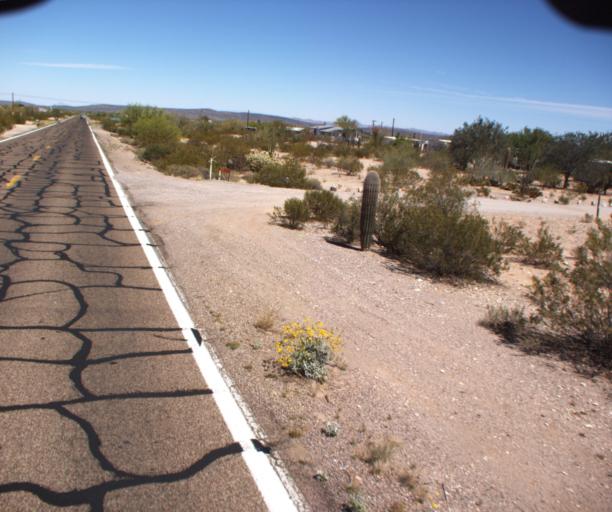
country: US
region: Arizona
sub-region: Pima County
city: Ajo
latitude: 32.4058
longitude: -112.8718
